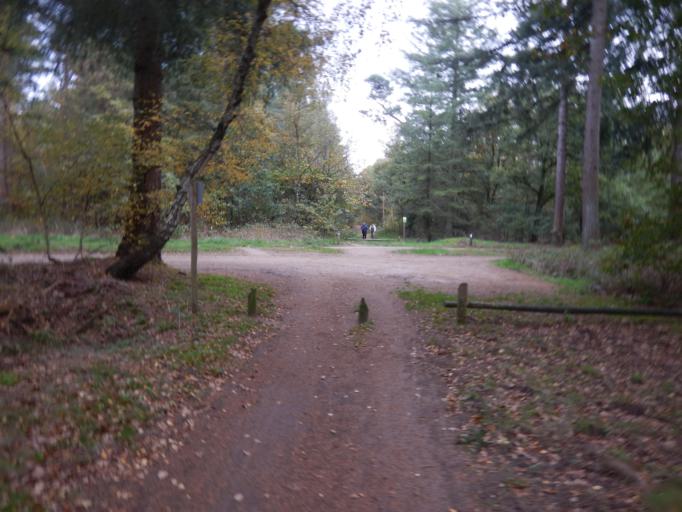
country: NL
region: Gelderland
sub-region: Gemeente Ermelo
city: Ermelo
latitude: 52.2859
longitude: 5.6288
